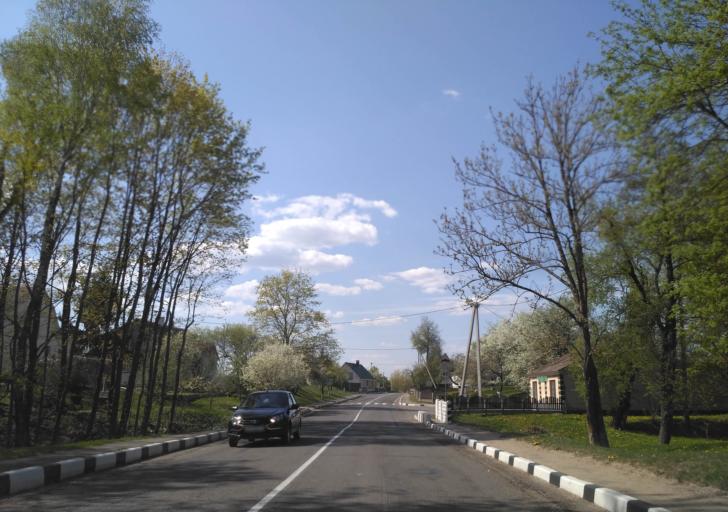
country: BY
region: Minsk
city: Narach
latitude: 54.8900
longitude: 26.7771
